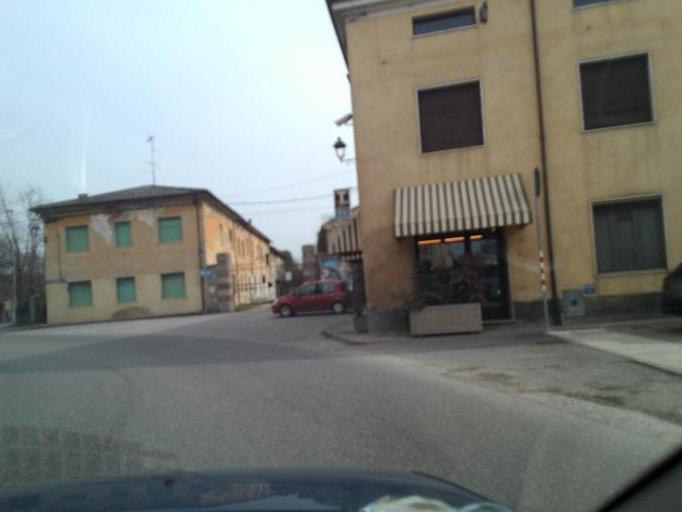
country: IT
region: Lombardy
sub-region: Provincia di Mantova
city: Roverbella
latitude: 45.2552
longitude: 10.7359
